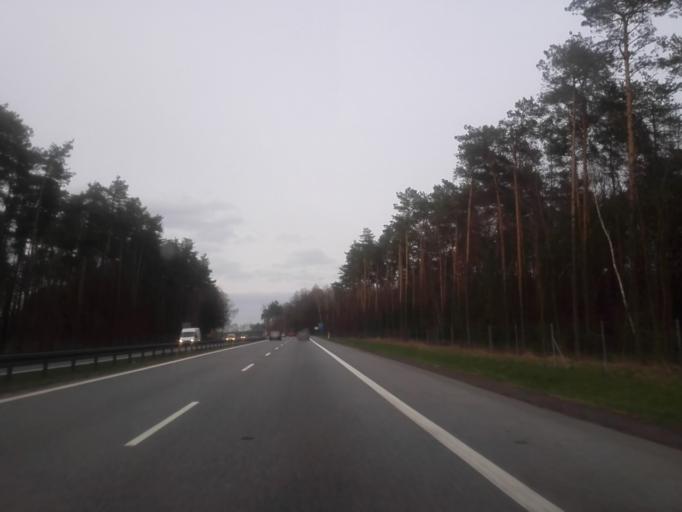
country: PL
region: Lodz Voivodeship
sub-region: Powiat skierniewicki
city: Kowiesy
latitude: 51.9300
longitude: 20.4698
